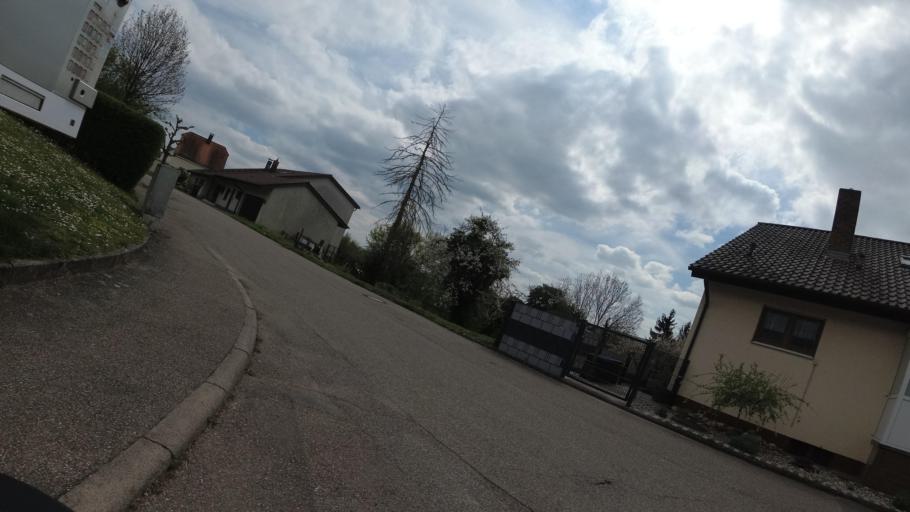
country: DE
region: Baden-Wuerttemberg
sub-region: Regierungsbezirk Stuttgart
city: Neuenstadt am Kocher
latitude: 49.2433
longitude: 9.3397
